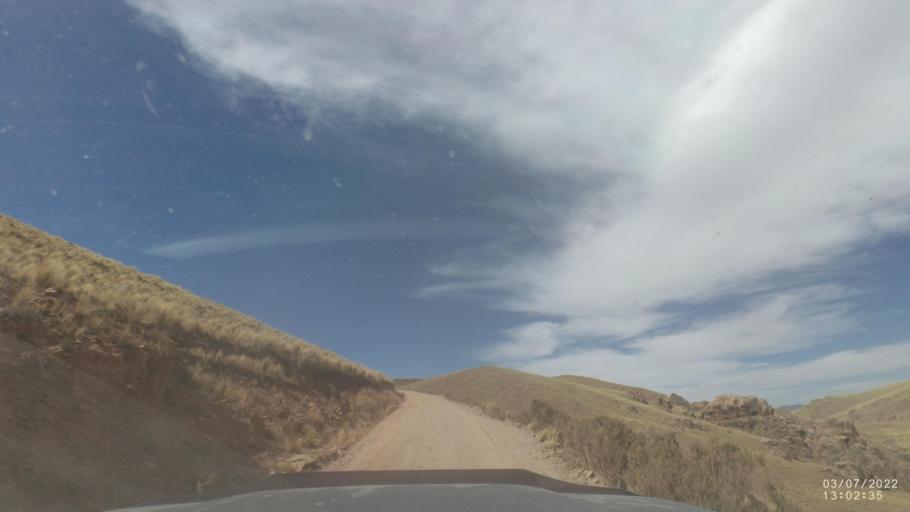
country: BO
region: Cochabamba
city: Colchani
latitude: -17.7064
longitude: -66.6915
